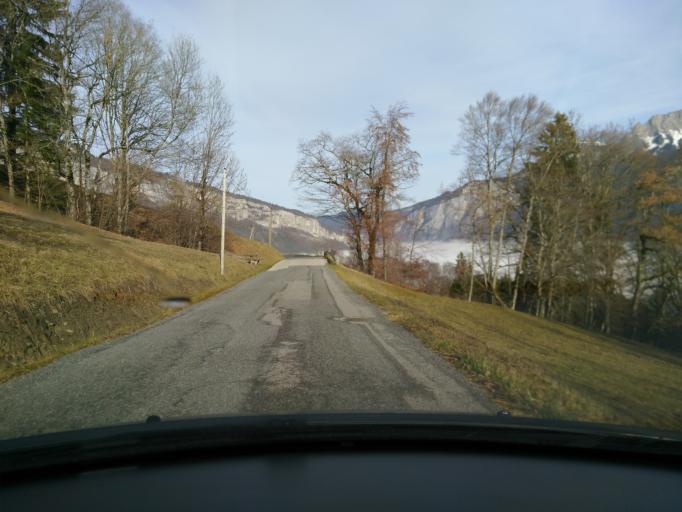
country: FR
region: Rhone-Alpes
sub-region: Departement de la Haute-Savoie
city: Sallanches
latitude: 45.9565
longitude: 6.6133
